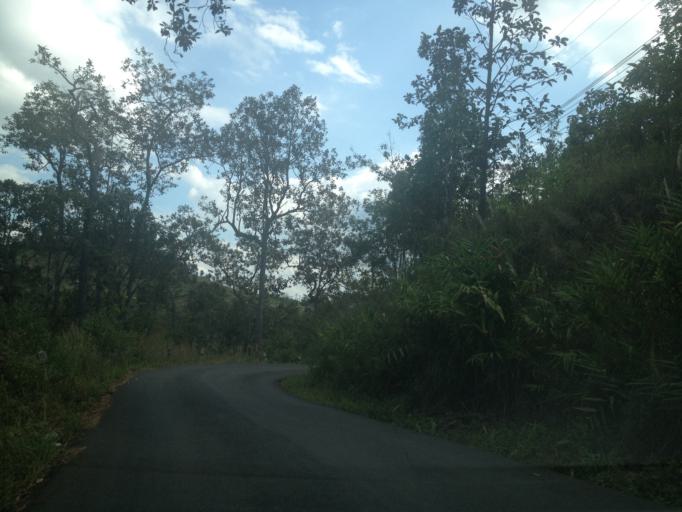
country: TH
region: Mae Hong Son
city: Ban Huai I Huak
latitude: 18.1392
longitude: 98.2181
